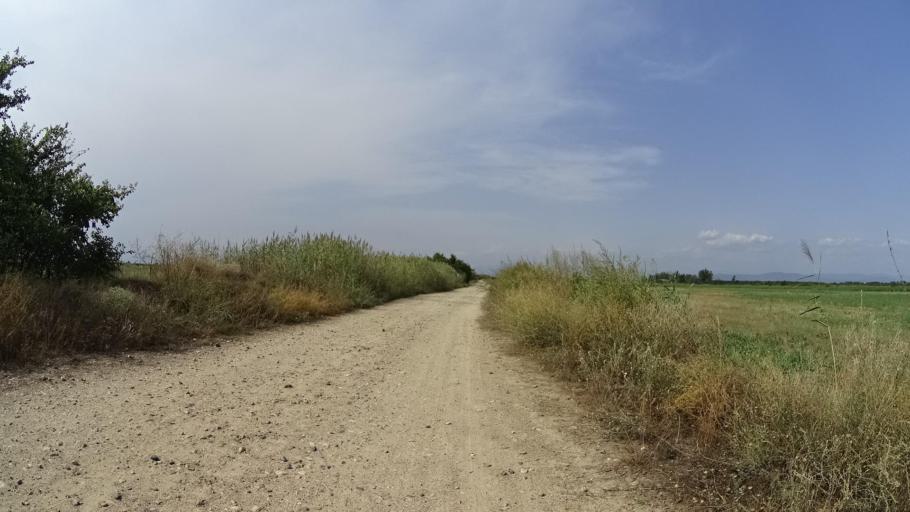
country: BG
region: Plovdiv
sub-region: Obshtina Kaloyanovo
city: Kaloyanovo
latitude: 42.2904
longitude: 24.7964
